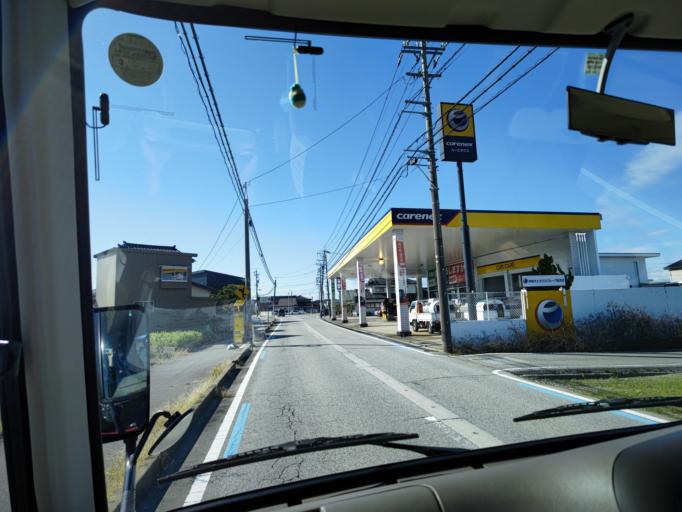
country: JP
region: Toyama
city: Nyuzen
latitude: 36.8985
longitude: 137.4205
